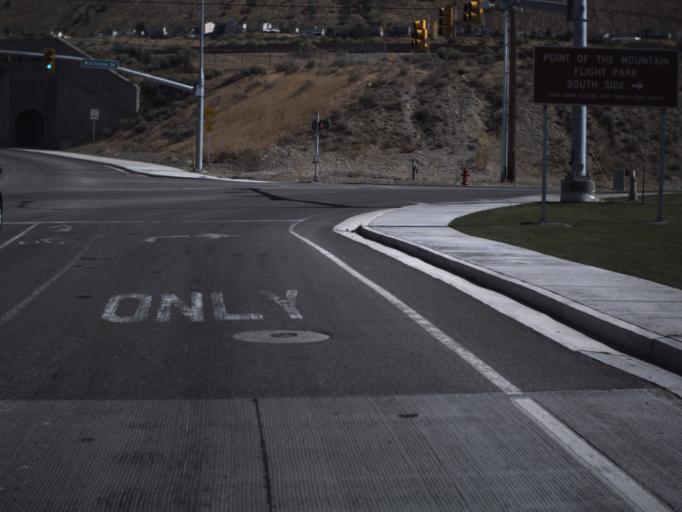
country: US
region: Utah
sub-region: Salt Lake County
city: Bluffdale
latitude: 40.4825
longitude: -111.8972
